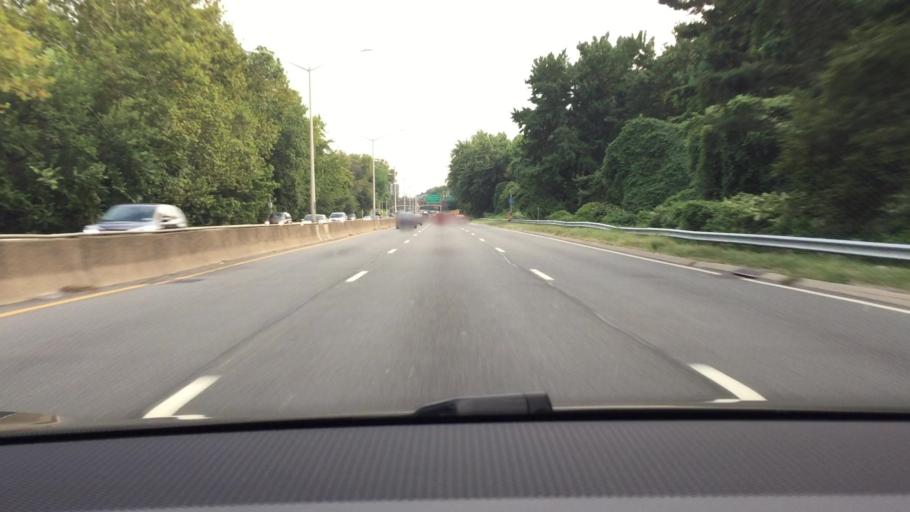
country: US
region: New York
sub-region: Bronx
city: The Bronx
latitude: 40.8832
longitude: -73.8683
